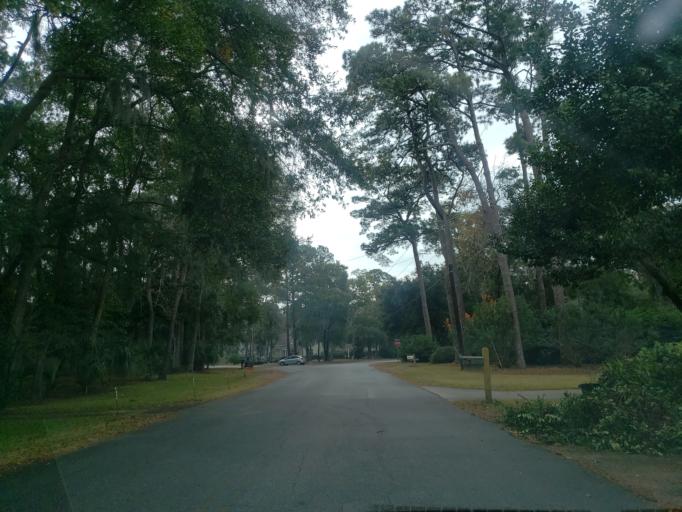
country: US
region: Georgia
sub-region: Chatham County
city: Wilmington Island
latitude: 31.9815
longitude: -80.9964
